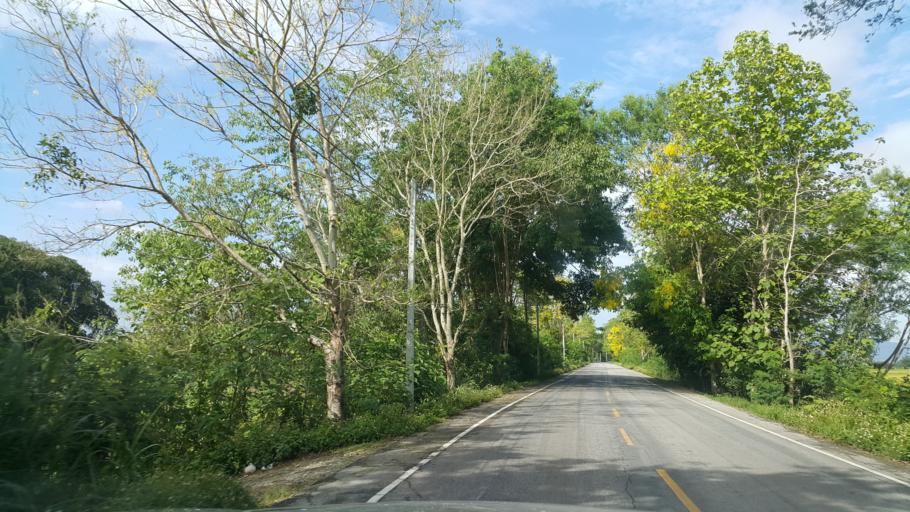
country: TH
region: Chiang Rai
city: Wiang Chai
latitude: 19.9342
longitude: 99.9110
